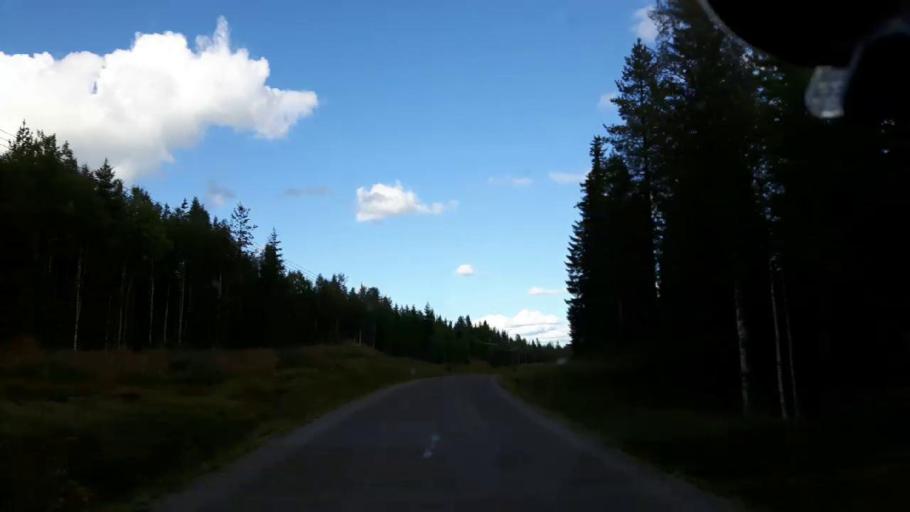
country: SE
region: Jaemtland
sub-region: Stroemsunds Kommun
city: Stroemsund
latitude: 63.4261
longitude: 15.8980
